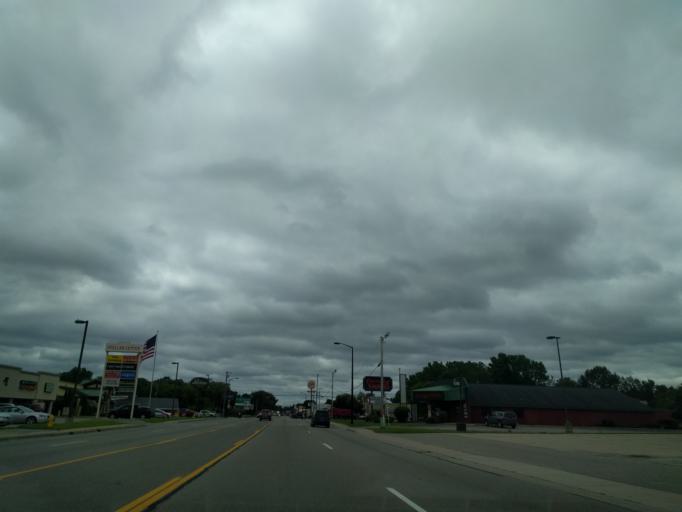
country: US
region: Michigan
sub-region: Menominee County
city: Menominee
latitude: 45.1207
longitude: -87.6136
